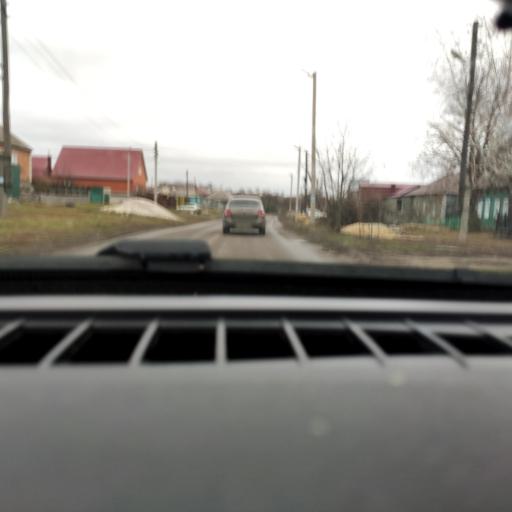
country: RU
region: Voronezj
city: Devitsa
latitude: 51.6393
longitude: 38.9368
